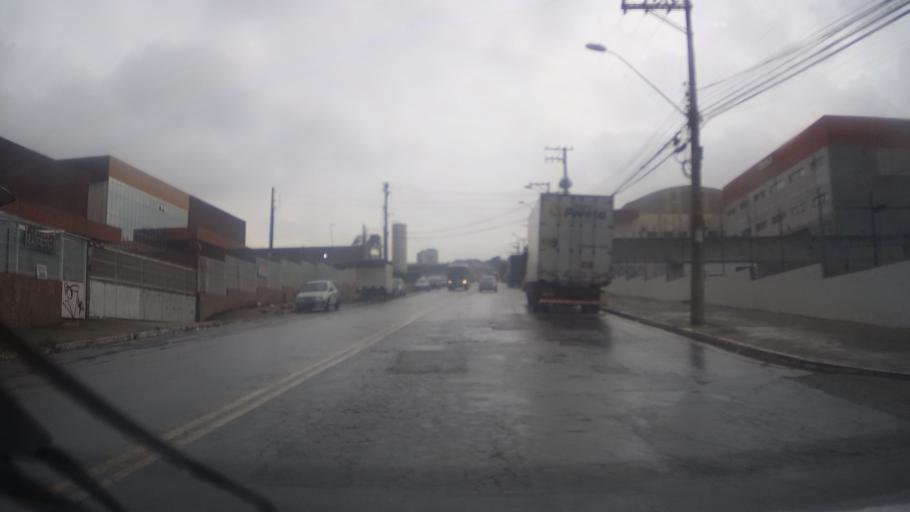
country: BR
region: Sao Paulo
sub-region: Guarulhos
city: Guarulhos
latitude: -23.4400
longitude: -46.5041
